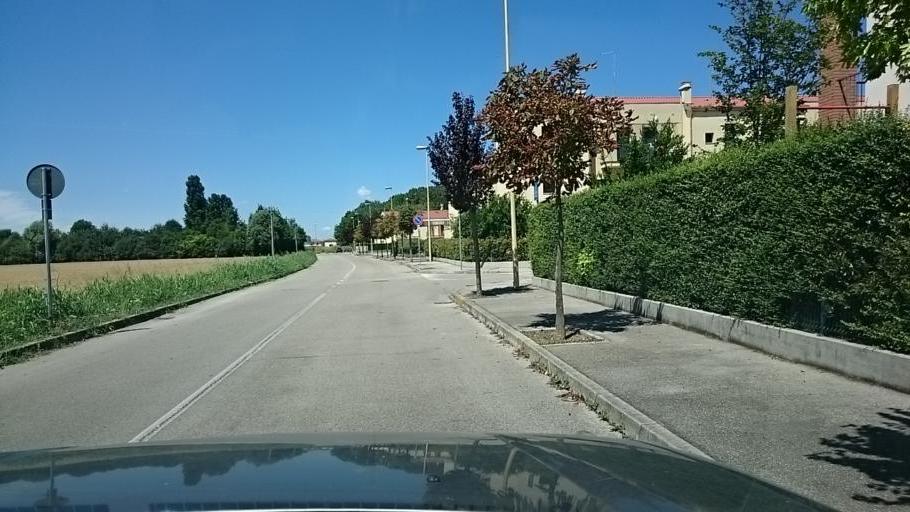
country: IT
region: Veneto
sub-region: Provincia di Padova
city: Ponte San Nicolo
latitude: 45.3630
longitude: 11.9270
